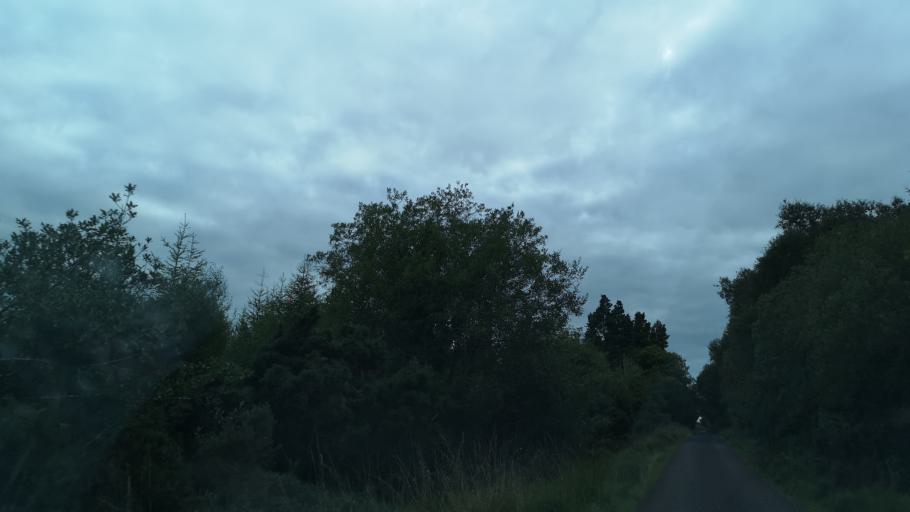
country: IE
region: Connaught
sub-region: County Galway
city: Loughrea
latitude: 53.1321
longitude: -8.5099
